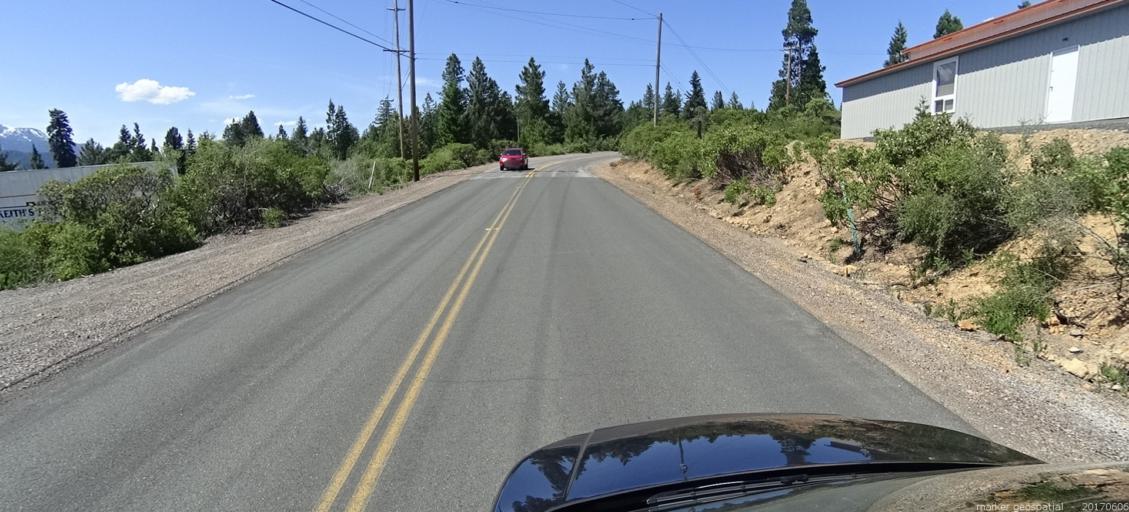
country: US
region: California
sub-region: Siskiyou County
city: Mount Shasta
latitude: 41.2854
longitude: -122.2995
